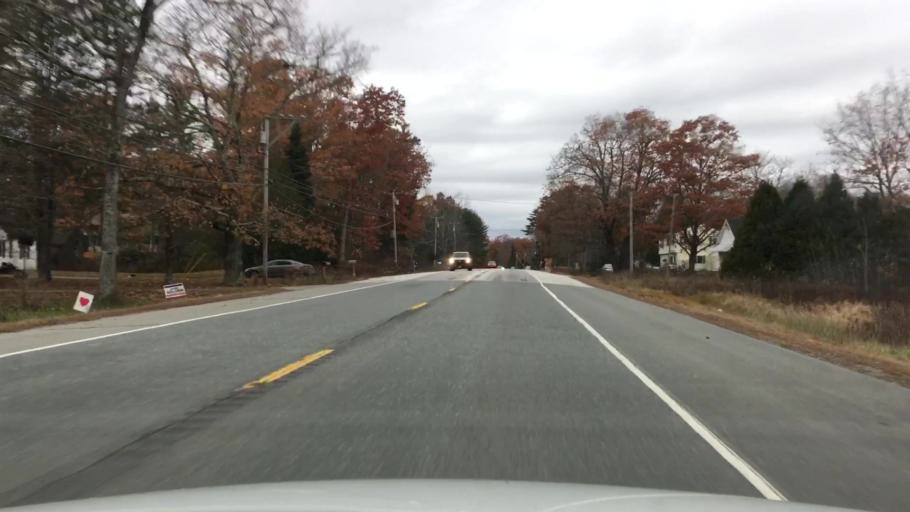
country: US
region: Maine
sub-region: Hancock County
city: Orland
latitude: 44.5630
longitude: -68.7137
